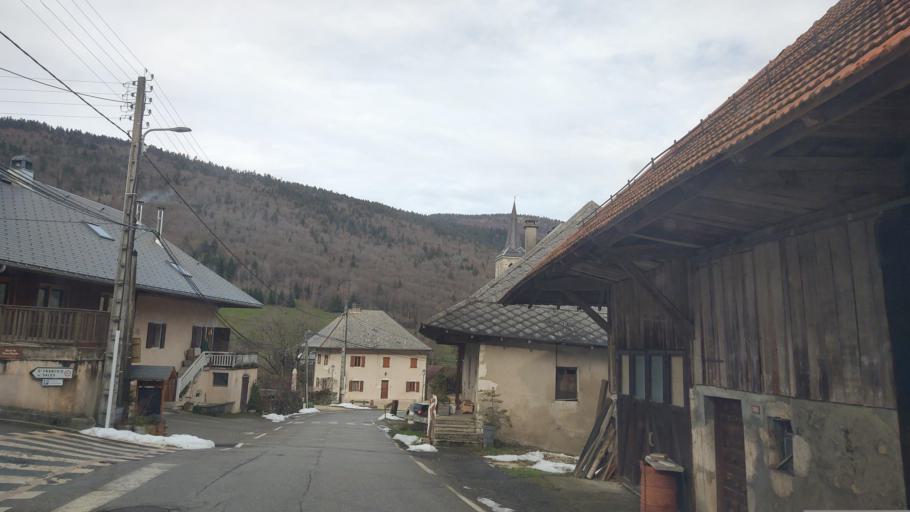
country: FR
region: Rhone-Alpes
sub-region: Departement de la Haute-Savoie
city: Cusy
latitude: 45.6788
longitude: 6.0609
